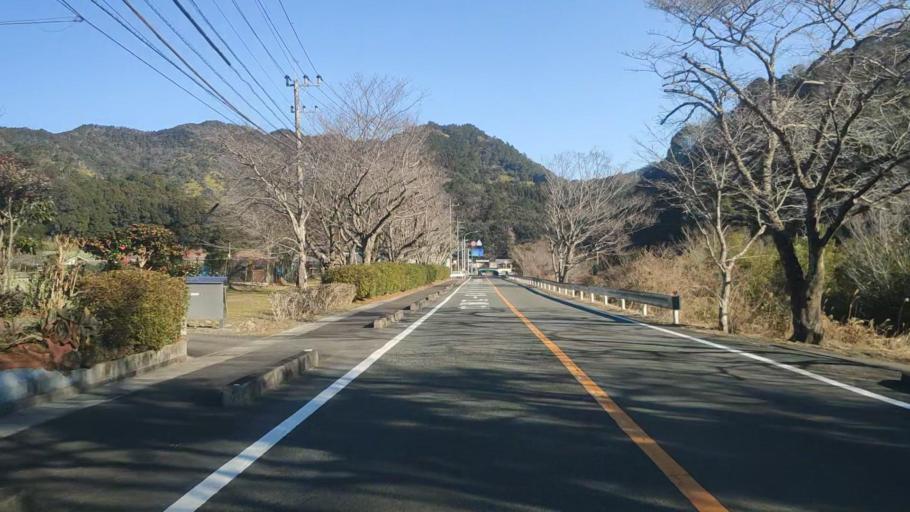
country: JP
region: Miyazaki
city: Nobeoka
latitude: 32.6431
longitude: 131.7452
